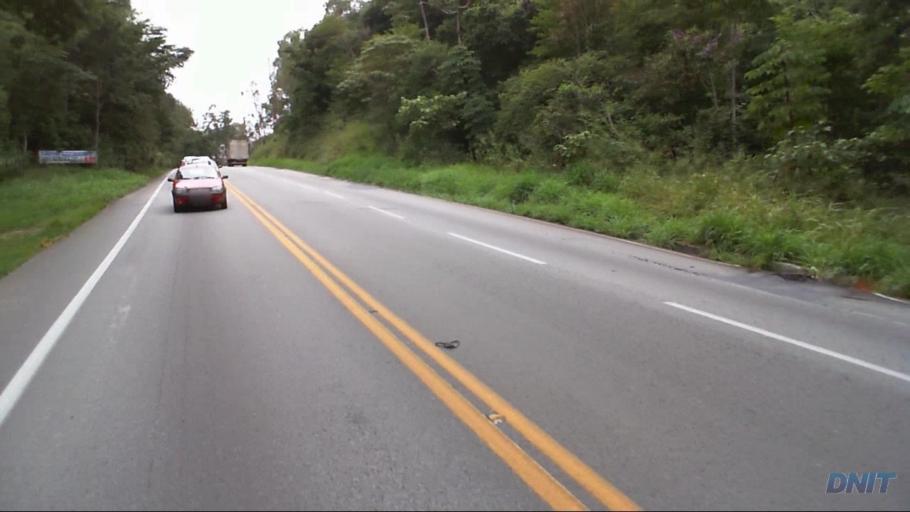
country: BR
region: Minas Gerais
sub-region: Joao Monlevade
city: Joao Monlevade
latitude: -19.8450
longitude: -43.1068
